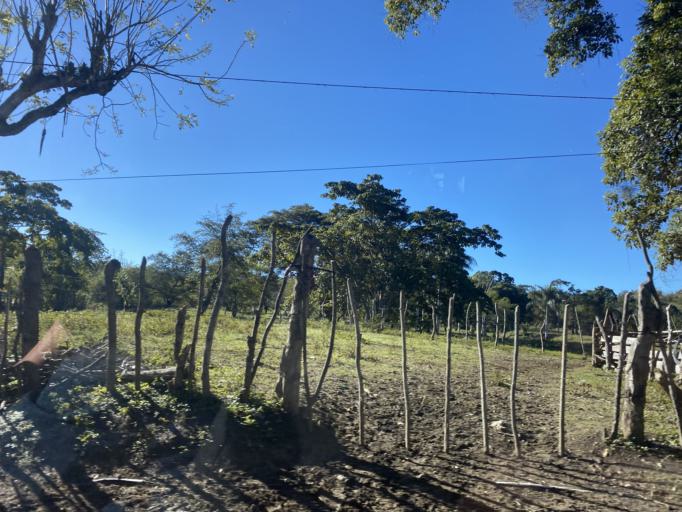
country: DO
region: Puerto Plata
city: Imbert
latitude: 19.7316
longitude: -70.8263
